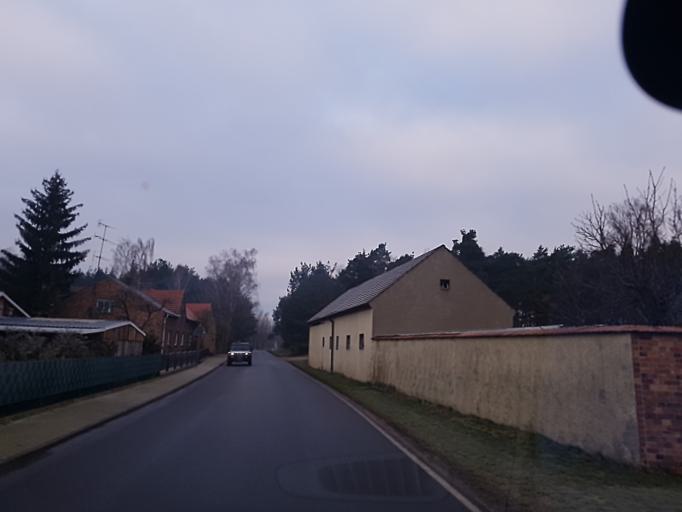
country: DE
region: Brandenburg
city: Finsterwalde
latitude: 51.6875
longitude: 13.7264
